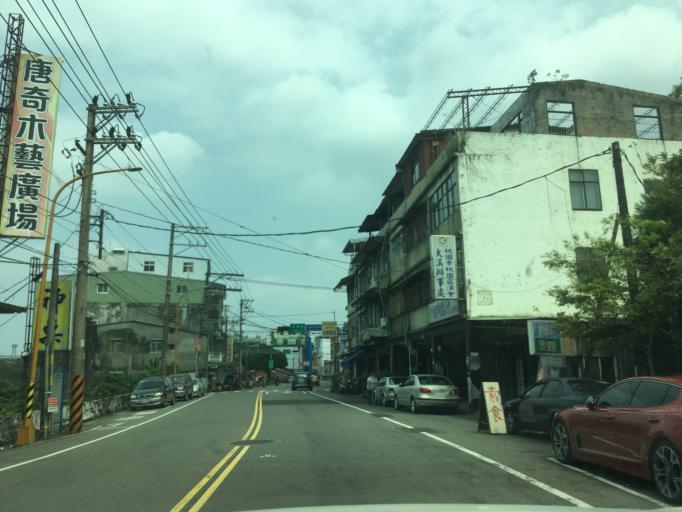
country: TW
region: Taiwan
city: Daxi
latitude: 24.8769
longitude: 121.2875
